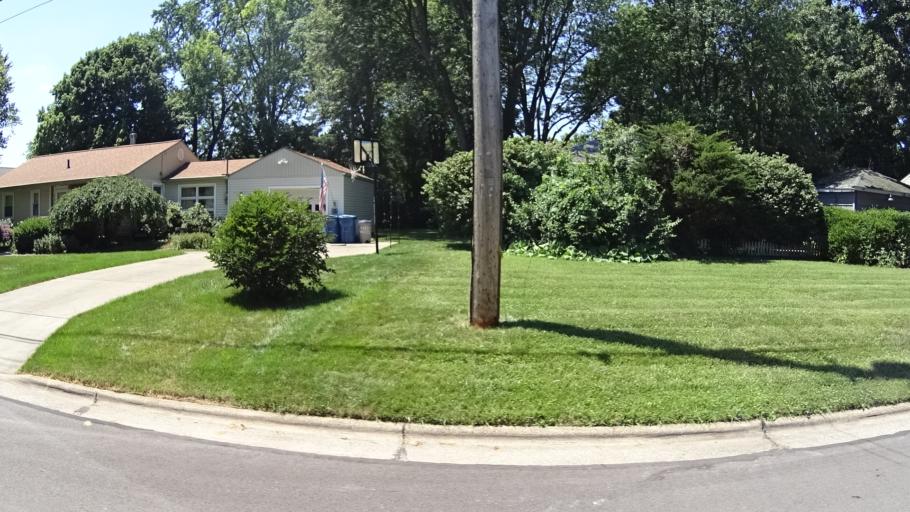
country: US
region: Ohio
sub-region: Erie County
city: Huron
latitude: 41.3924
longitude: -82.5675
